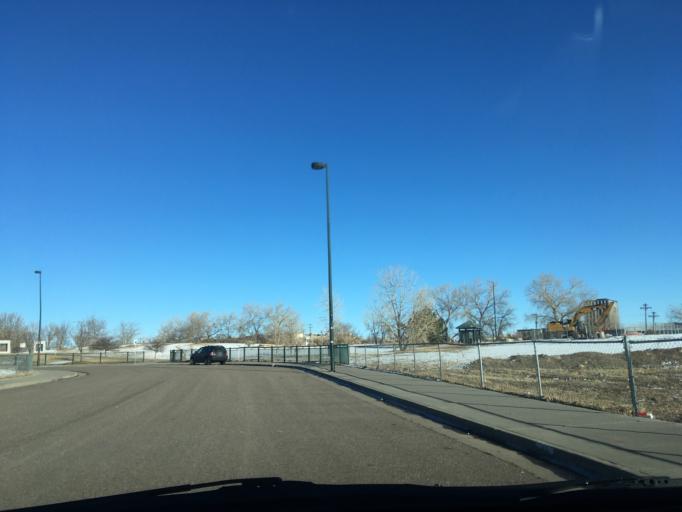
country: US
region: Colorado
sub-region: Adams County
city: Commerce City
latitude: 39.7889
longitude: -104.9745
